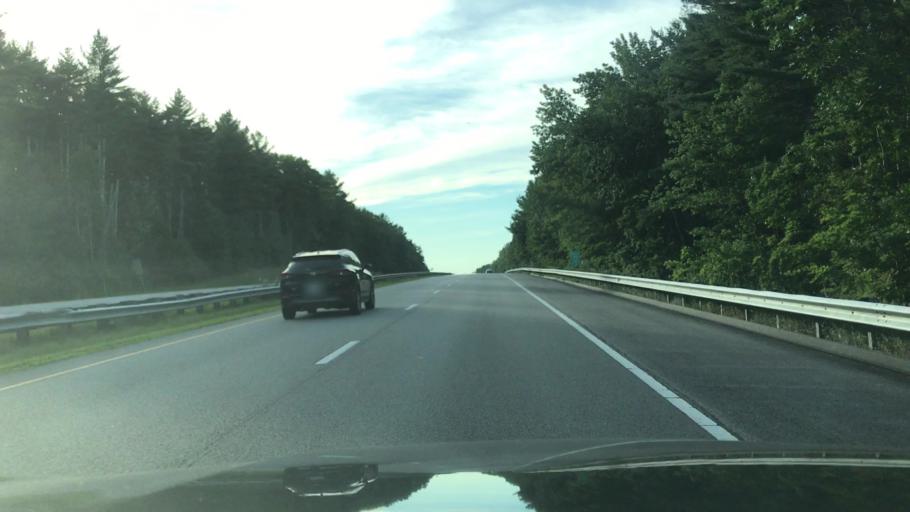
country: US
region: New Hampshire
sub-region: Strafford County
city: Somersworth
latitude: 43.2363
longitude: -70.9157
